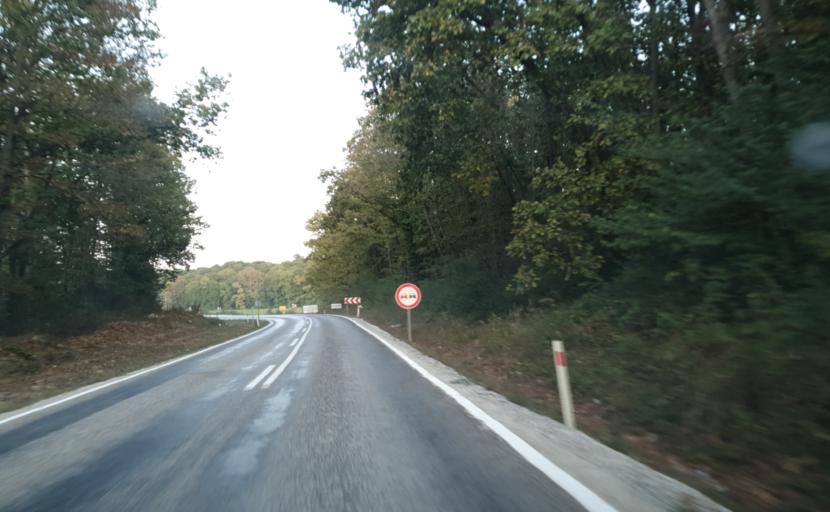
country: TR
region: Kirklareli
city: Igneada
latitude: 41.8718
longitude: 27.9329
